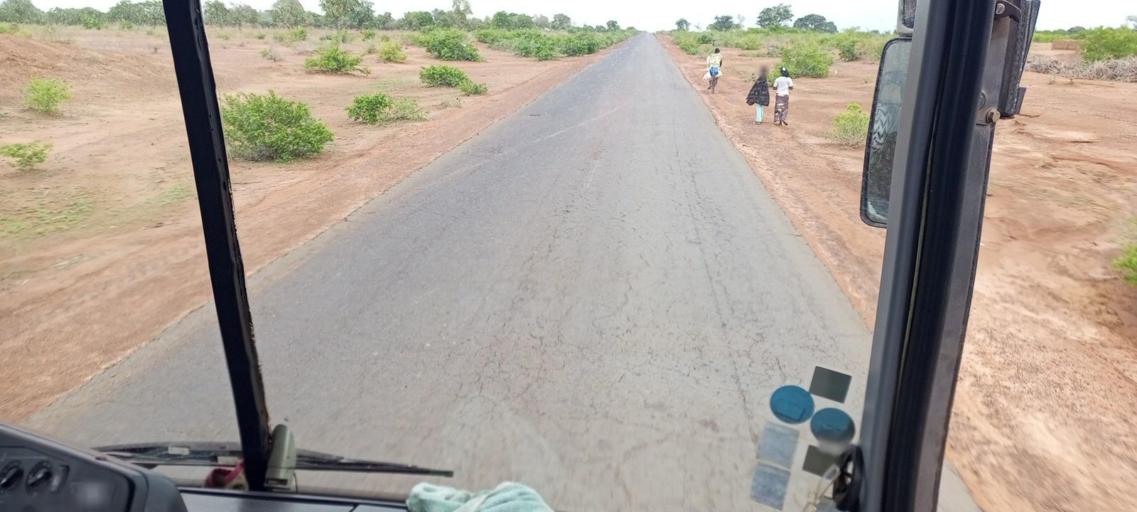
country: ML
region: Segou
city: Bla
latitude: 12.7189
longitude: -5.7248
